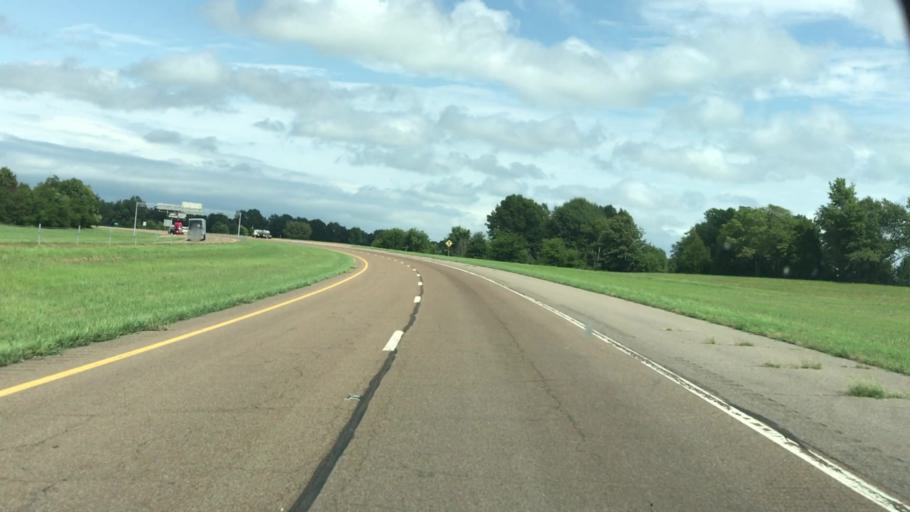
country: US
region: Tennessee
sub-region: Obion County
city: Union City
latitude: 36.4437
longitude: -89.0108
